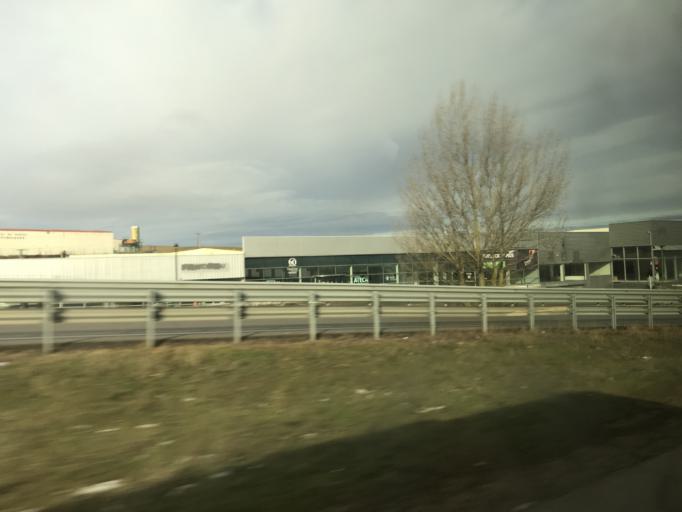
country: ES
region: Castille and Leon
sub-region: Provincia de Burgos
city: Burgos
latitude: 42.3237
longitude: -3.7010
